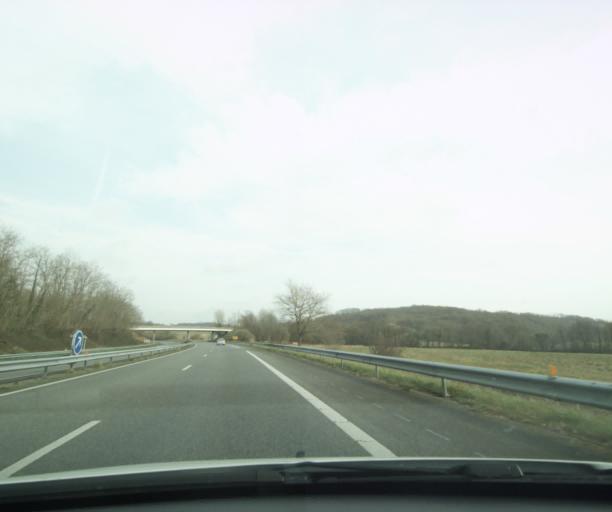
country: FR
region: Aquitaine
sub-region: Departement des Landes
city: Labatut
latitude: 43.5070
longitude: -1.0227
